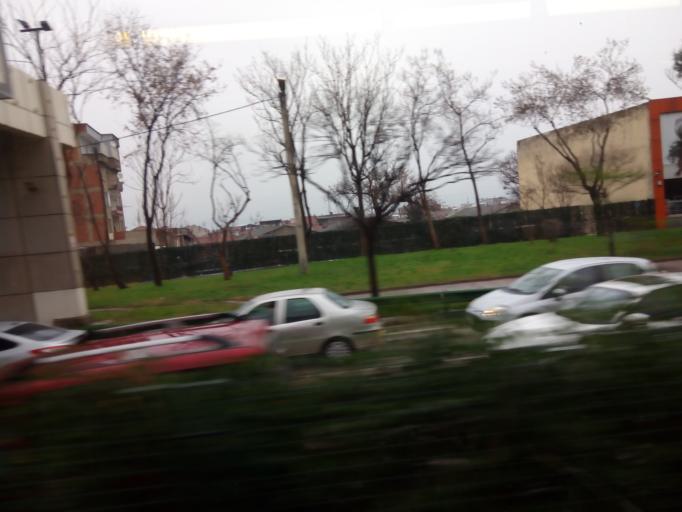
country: TR
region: Bursa
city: Yildirim
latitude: 40.2015
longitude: 29.0366
